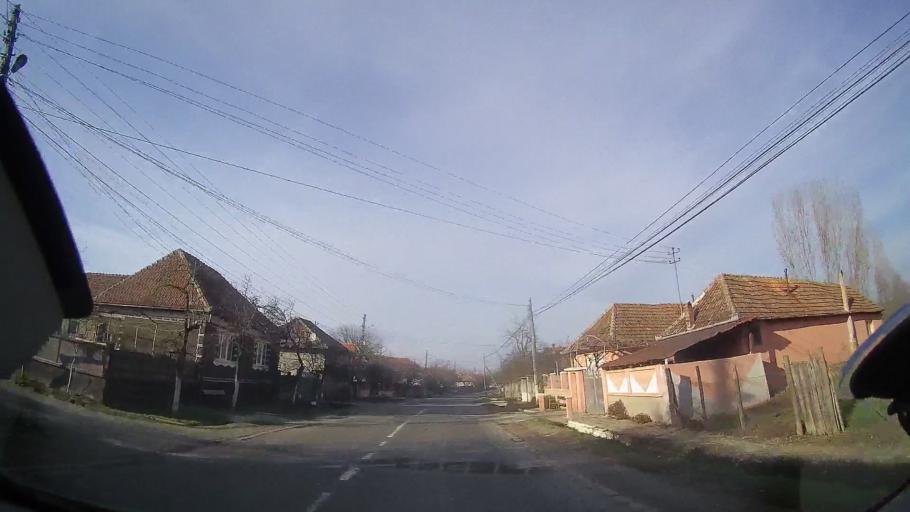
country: RO
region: Bihor
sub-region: Comuna Brusturi
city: Brusturi
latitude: 47.1454
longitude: 22.2576
